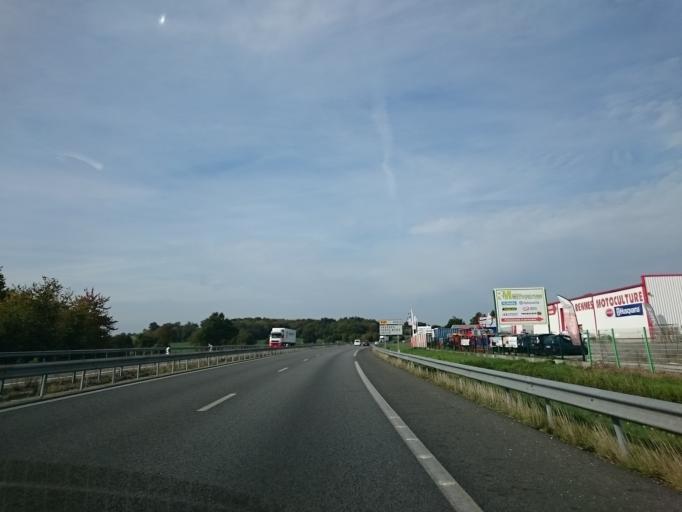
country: FR
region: Brittany
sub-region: Departement d'Ille-et-Vilaine
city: Laille
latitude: 47.9637
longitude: -1.6895
